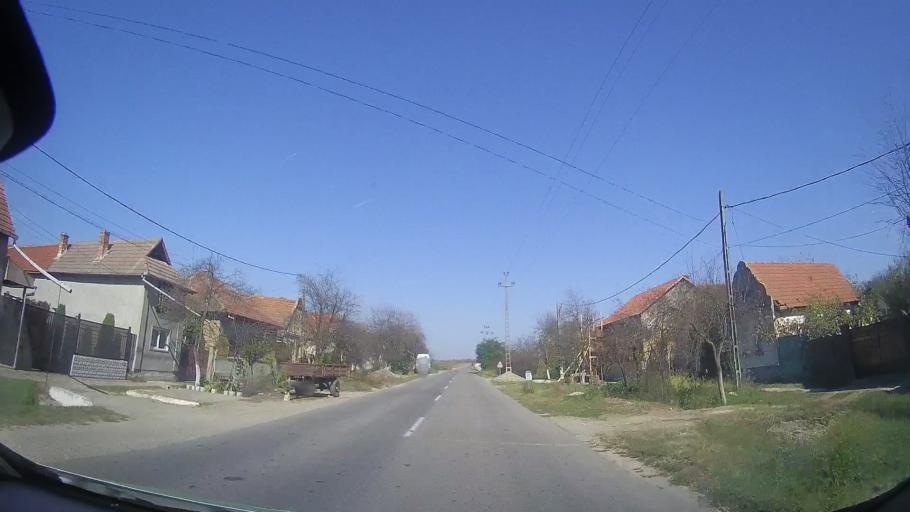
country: RO
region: Timis
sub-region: Comuna Costeiu
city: Costeiu
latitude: 45.7464
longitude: 21.8472
